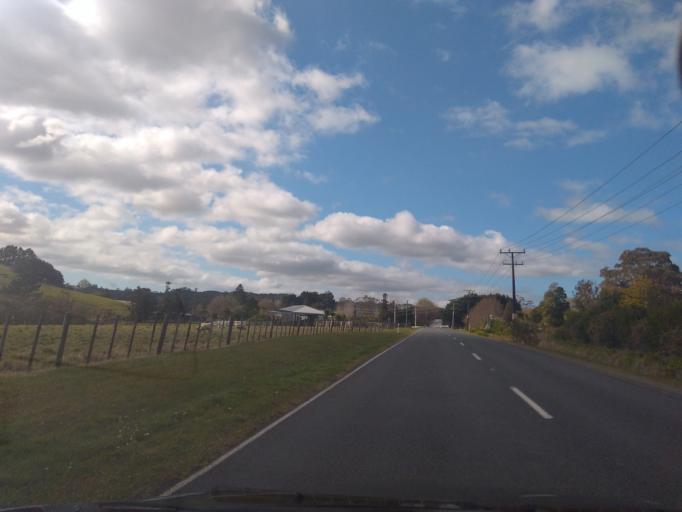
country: NZ
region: Northland
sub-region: Whangarei
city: Whangarei
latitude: -35.7000
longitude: 174.3473
